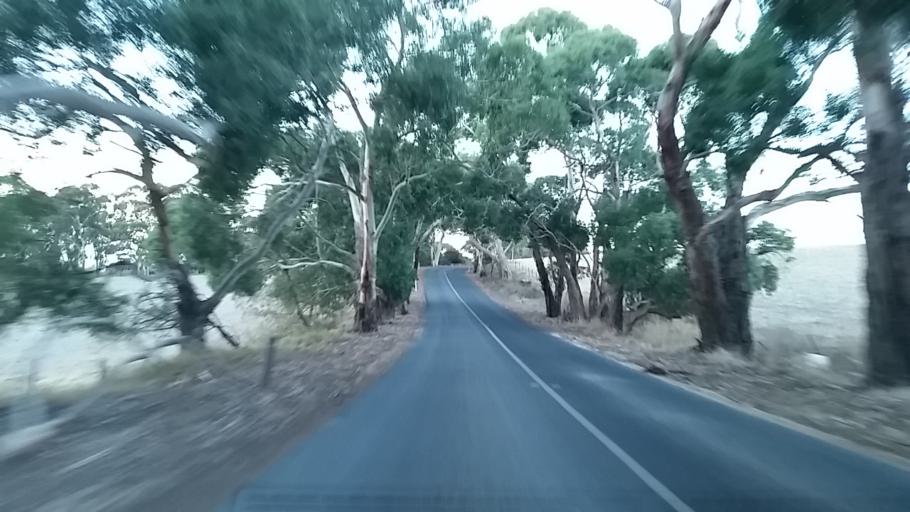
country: AU
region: South Australia
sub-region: Mount Barker
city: Nairne
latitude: -35.0608
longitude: 138.9256
